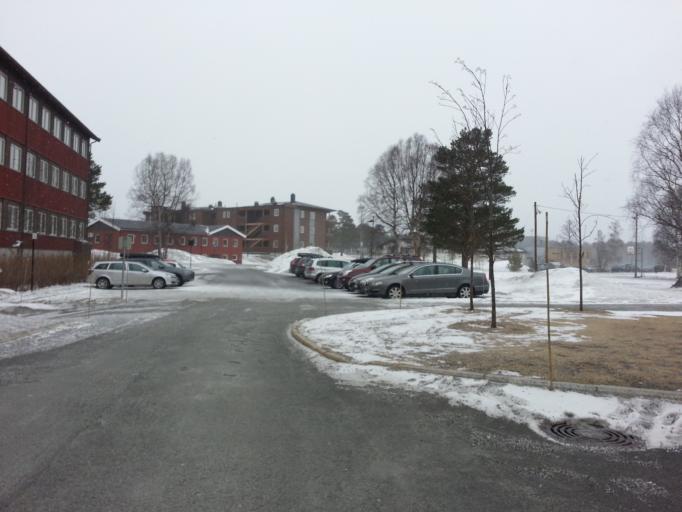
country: NO
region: Sor-Trondelag
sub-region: Oppdal
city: Oppdal
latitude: 62.5952
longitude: 9.6872
